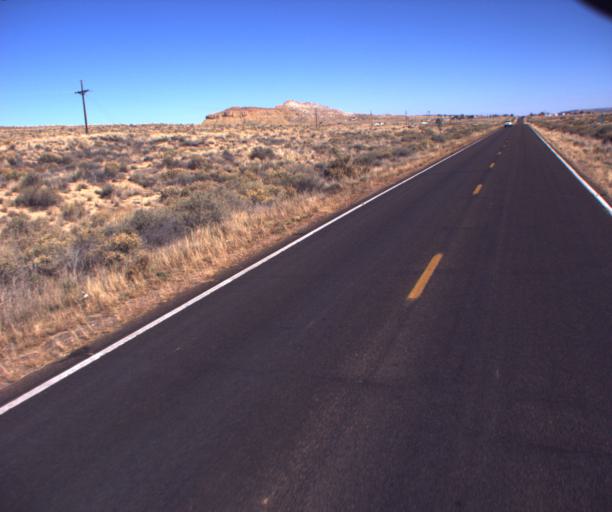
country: US
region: Arizona
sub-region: Navajo County
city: First Mesa
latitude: 35.8083
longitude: -110.4160
